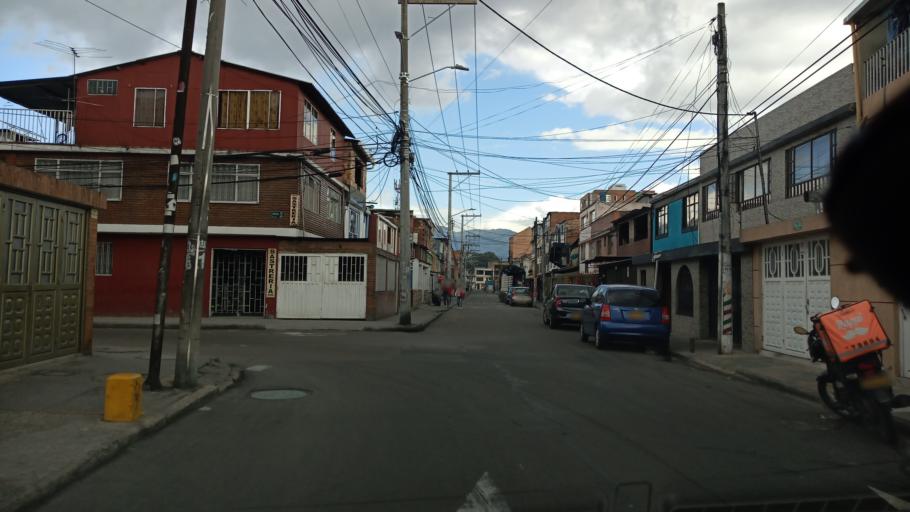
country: CO
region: Bogota D.C.
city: Bogota
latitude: 4.6827
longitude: -74.0954
